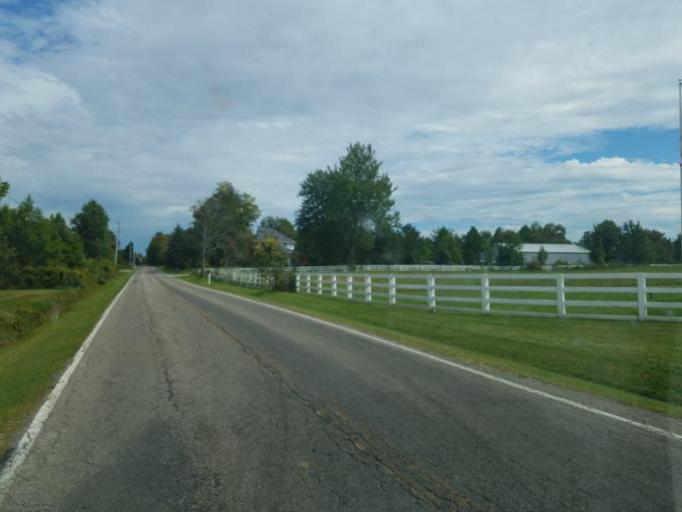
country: US
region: Ohio
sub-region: Licking County
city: Johnstown
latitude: 40.0960
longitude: -82.7241
